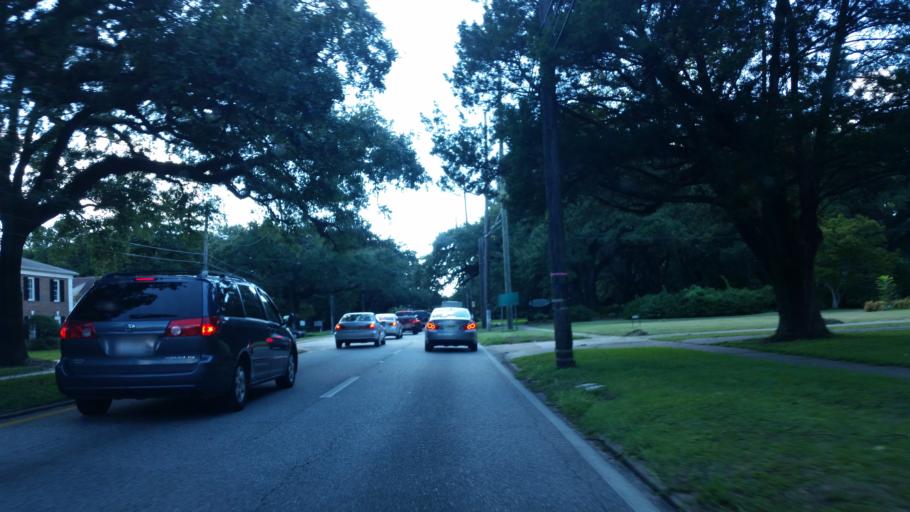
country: US
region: Alabama
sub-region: Mobile County
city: Mobile
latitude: 30.6919
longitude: -88.0849
